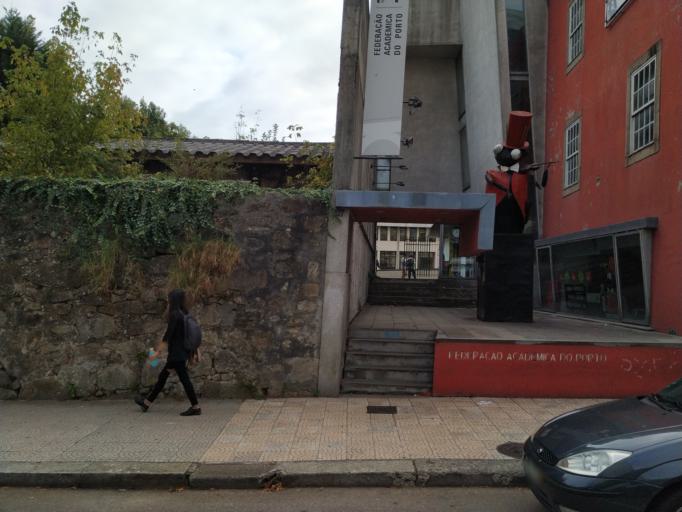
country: PT
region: Porto
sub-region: Porto
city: Porto
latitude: 41.1525
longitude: -8.6359
